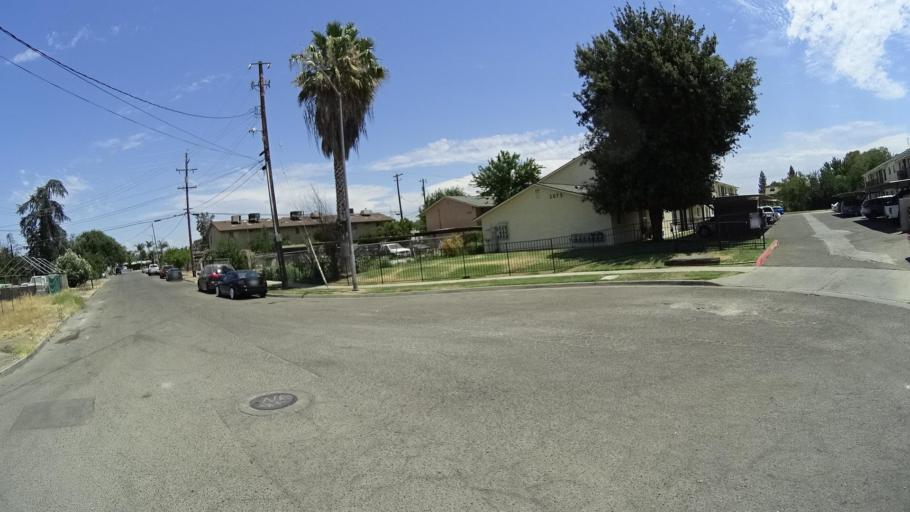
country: US
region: California
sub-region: Fresno County
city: Fresno
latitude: 36.7218
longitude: -119.7489
